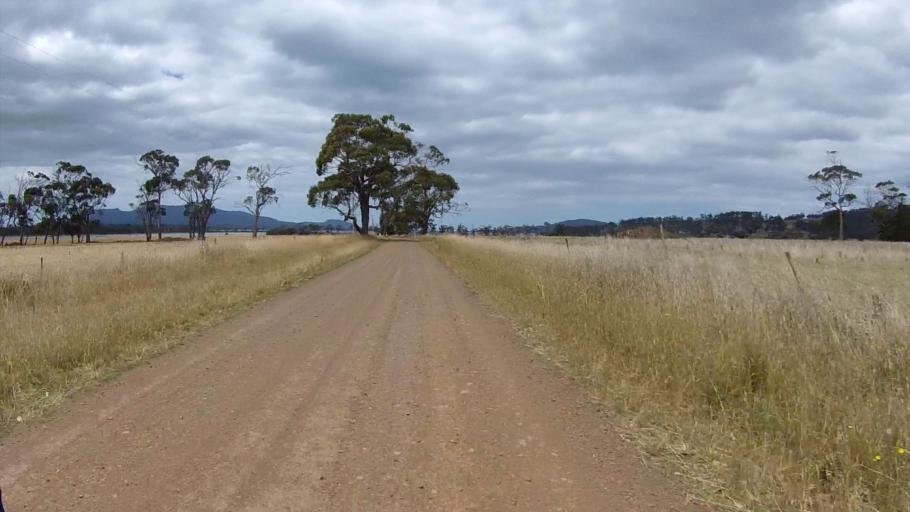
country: AU
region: Tasmania
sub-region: Sorell
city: Sorell
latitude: -42.6545
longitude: 147.9304
